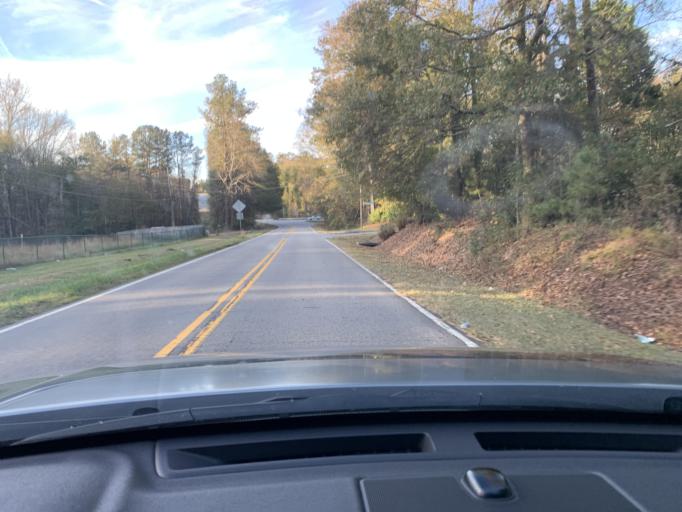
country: US
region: Georgia
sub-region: Oconee County
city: Bogart
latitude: 33.9282
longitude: -83.4593
